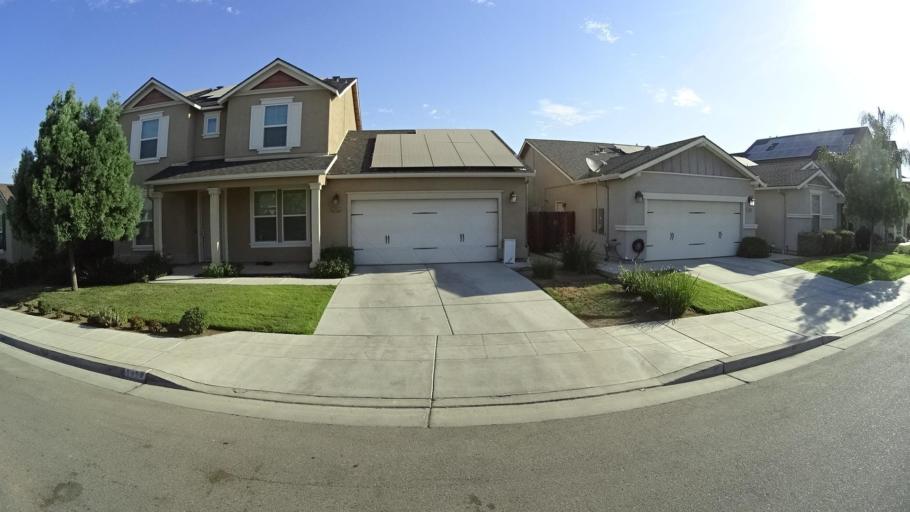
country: US
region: California
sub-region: Fresno County
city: Tarpey Village
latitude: 36.7883
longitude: -119.6657
